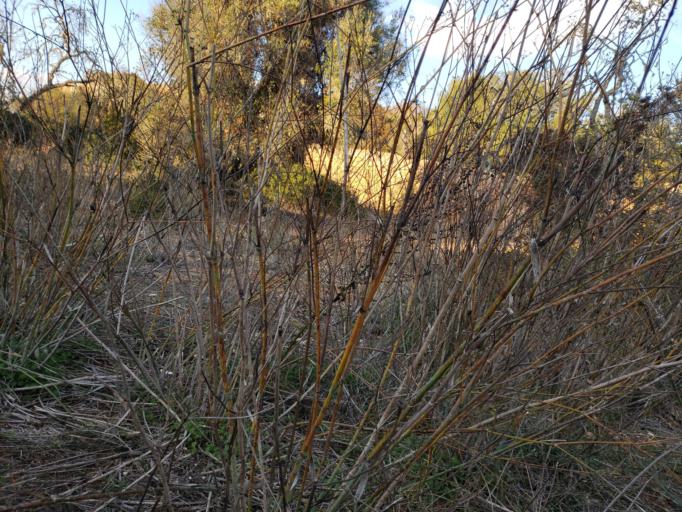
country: PT
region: Faro
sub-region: Portimao
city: Alvor
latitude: 37.1328
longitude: -8.5949
